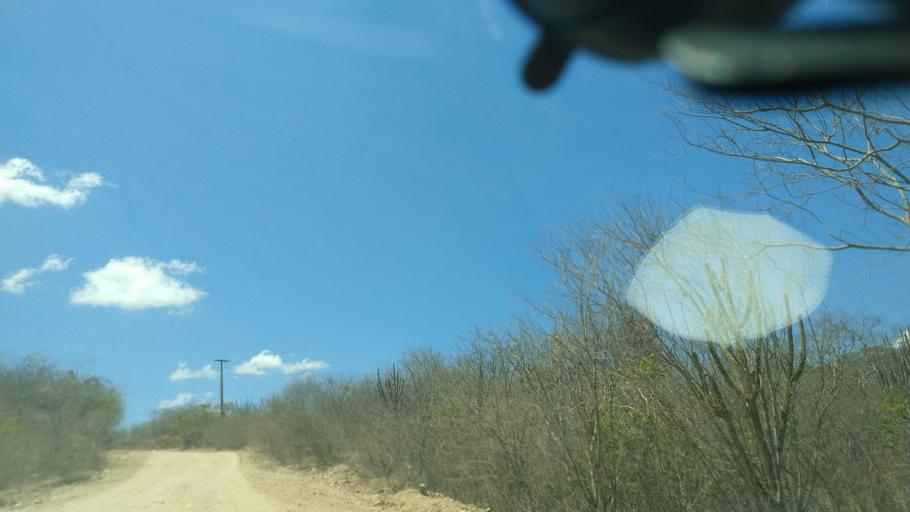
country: BR
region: Rio Grande do Norte
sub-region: Cerro Cora
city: Cerro Cora
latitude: -6.0120
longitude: -36.3249
